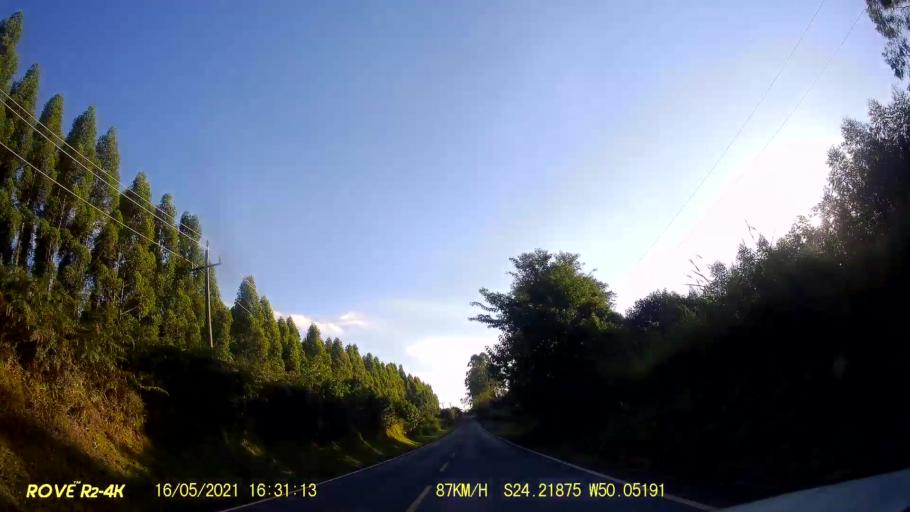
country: BR
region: Parana
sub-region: Pirai Do Sul
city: Pirai do Sul
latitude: -24.2188
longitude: -50.0521
